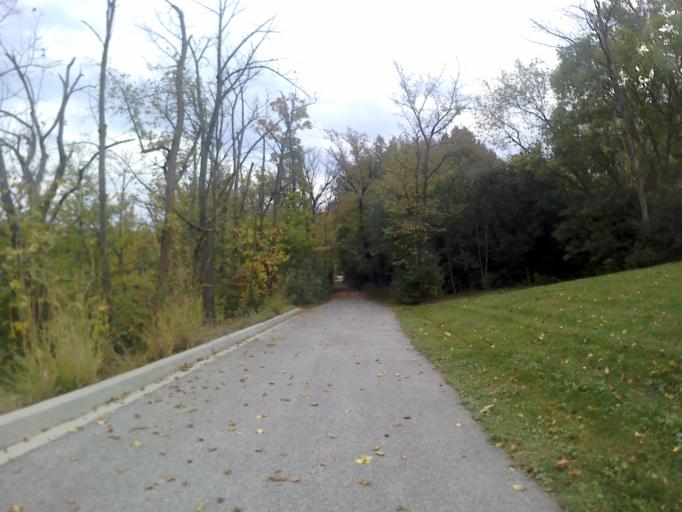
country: US
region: Illinois
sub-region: DuPage County
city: Naperville
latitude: 41.7803
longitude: -88.1733
